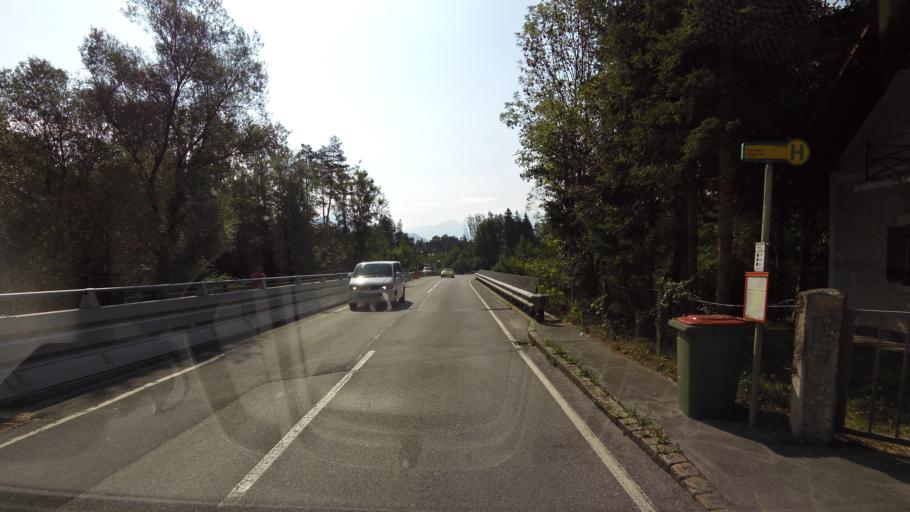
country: AT
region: Salzburg
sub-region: Politischer Bezirk Hallein
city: Adnet
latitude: 47.6562
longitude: 13.1271
